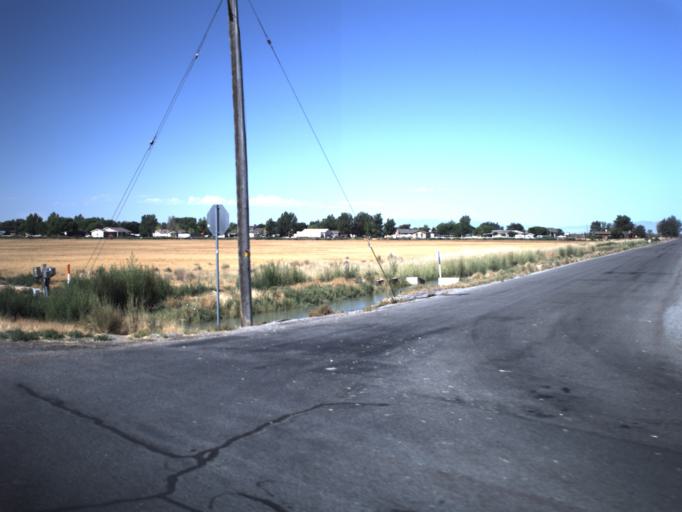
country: US
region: Utah
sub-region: Millard County
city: Delta
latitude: 39.3380
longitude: -112.6064
